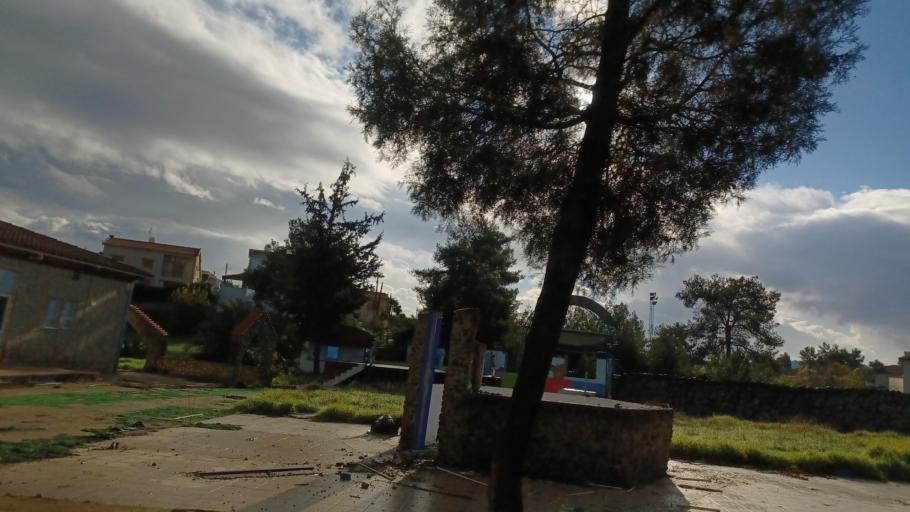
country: CY
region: Lefkosia
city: Lythrodontas
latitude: 34.9605
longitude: 33.3326
